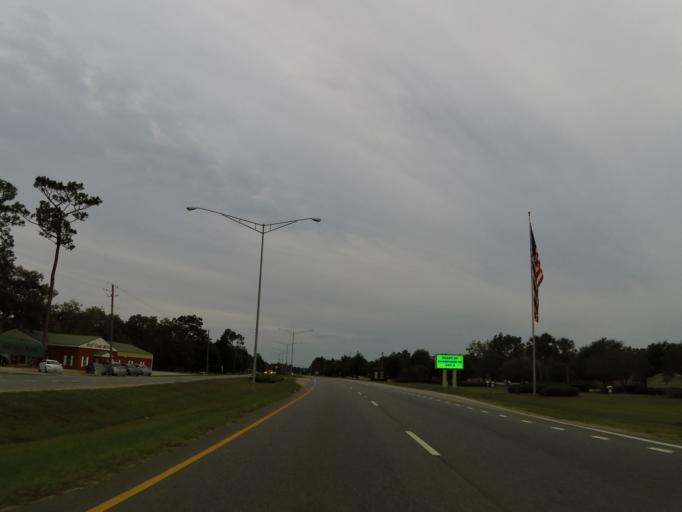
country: US
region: Alabama
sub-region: Baldwin County
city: Bay Minette
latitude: 30.8524
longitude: -87.7766
